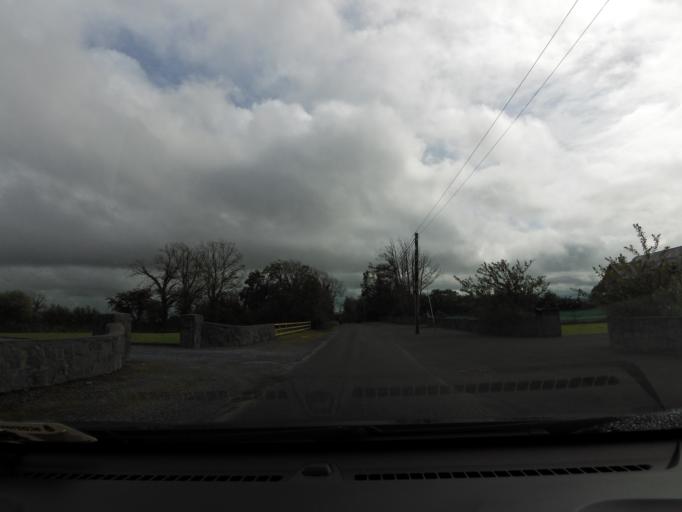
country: IE
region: Connaught
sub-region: County Galway
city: Loughrea
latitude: 53.3056
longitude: -8.6171
